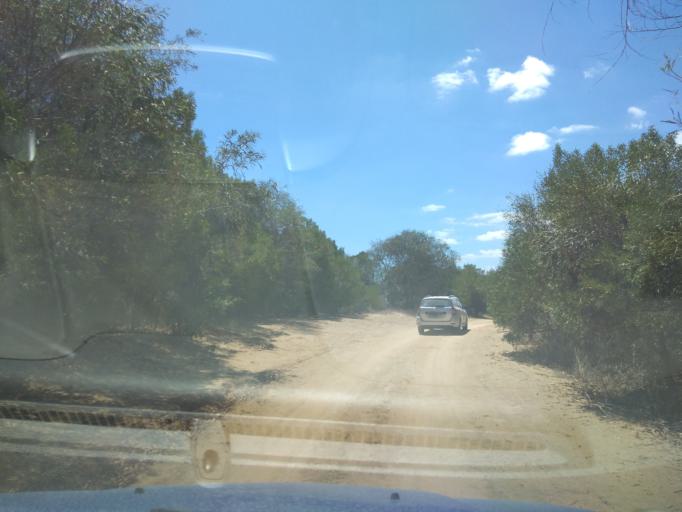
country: TN
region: Susah
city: Harqalah
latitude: 36.1620
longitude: 10.4638
